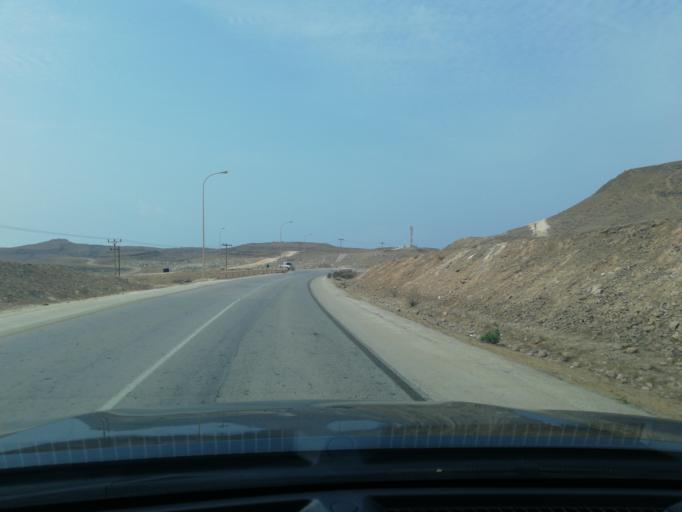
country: OM
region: Zufar
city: Salalah
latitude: 16.9200
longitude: 53.8426
